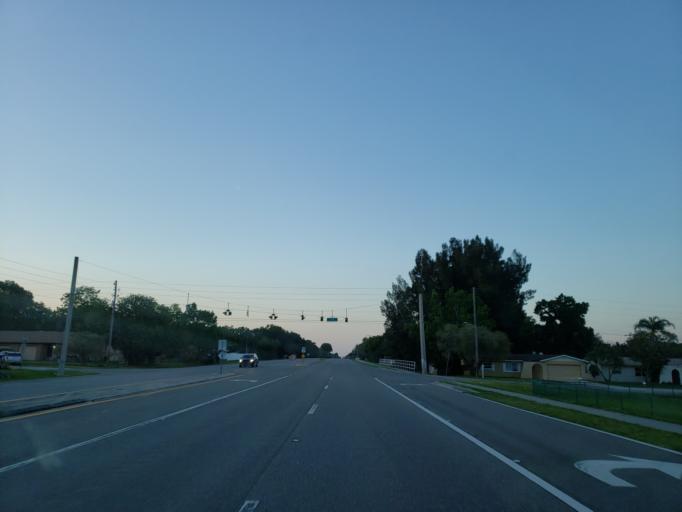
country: US
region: Florida
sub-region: Pinellas County
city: Ridgecrest
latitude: 27.8723
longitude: -82.7952
